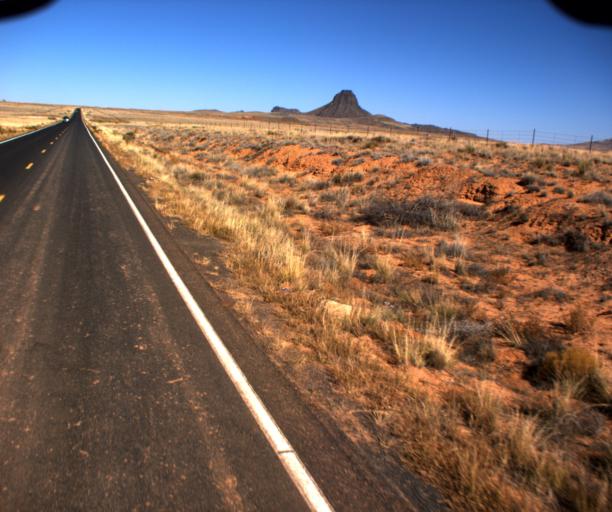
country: US
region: Arizona
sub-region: Navajo County
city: Dilkon
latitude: 35.2666
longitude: -110.4294
